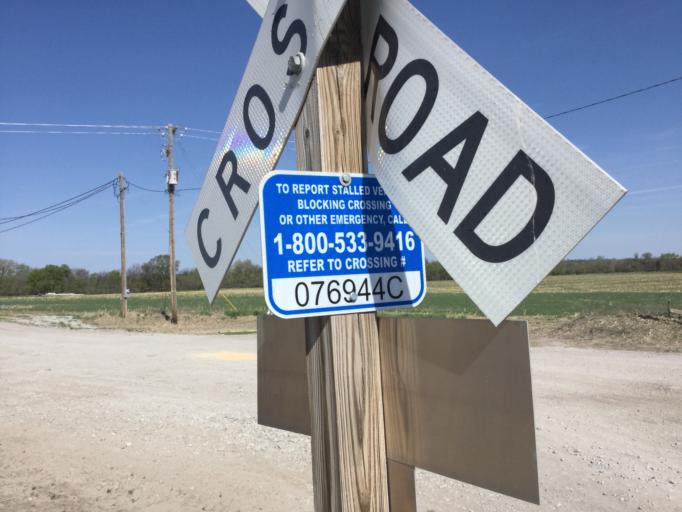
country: US
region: Kansas
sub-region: Decatur County
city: Oberlin
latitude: 39.9805
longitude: -100.5620
